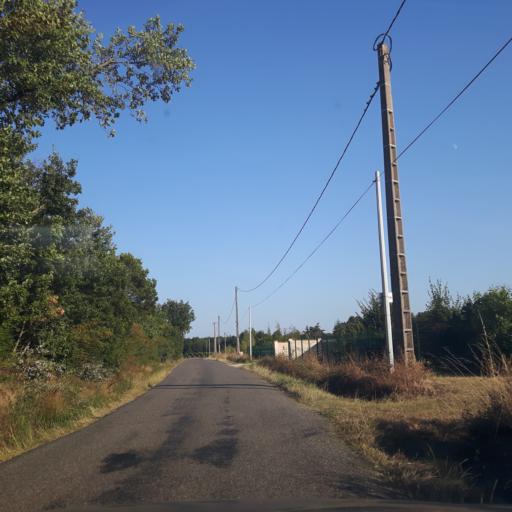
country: FR
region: Midi-Pyrenees
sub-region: Departement de la Haute-Garonne
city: Villaudric
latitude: 43.7999
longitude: 1.4482
